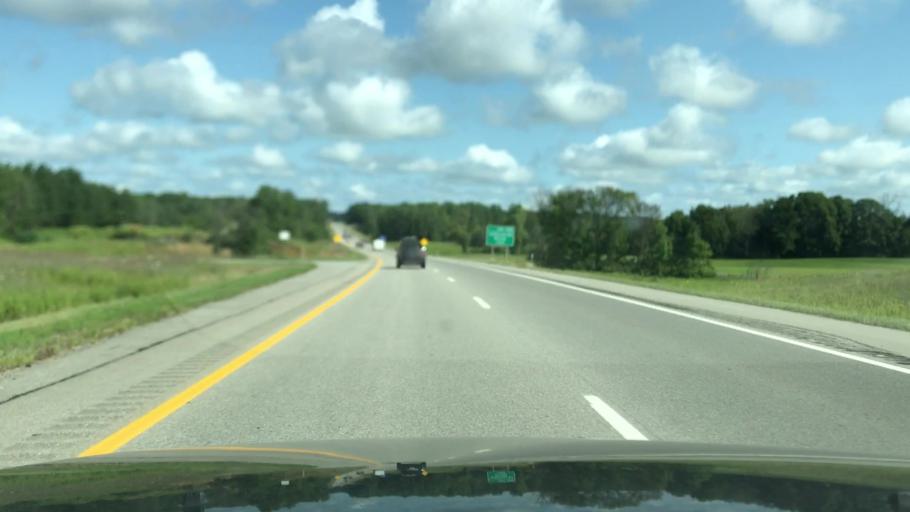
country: US
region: Michigan
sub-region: Montcalm County
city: Howard City
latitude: 43.4688
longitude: -85.4762
